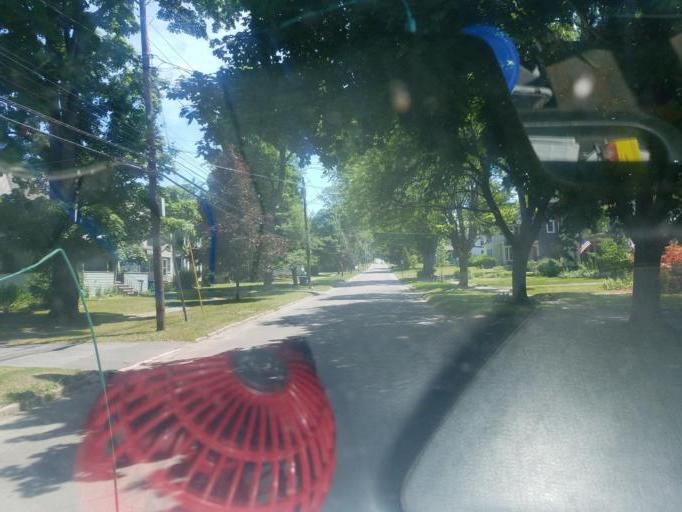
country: US
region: New York
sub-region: Yates County
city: Penn Yan
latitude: 42.6566
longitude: -77.0478
